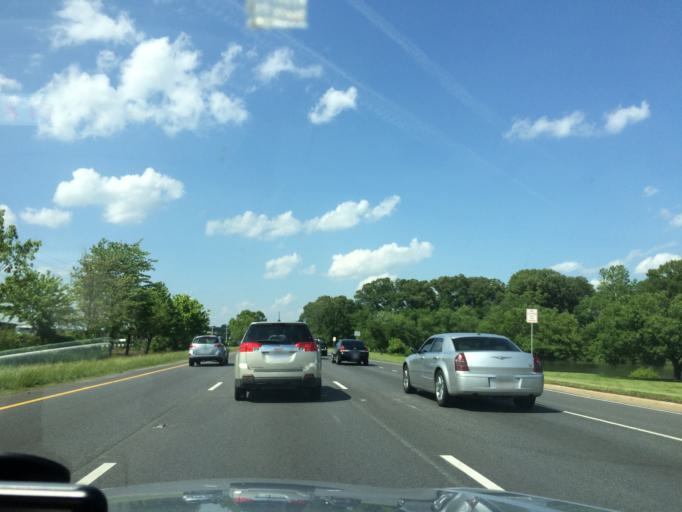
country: US
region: Maryland
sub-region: Anne Arundel County
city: Crofton
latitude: 39.0103
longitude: -76.6978
